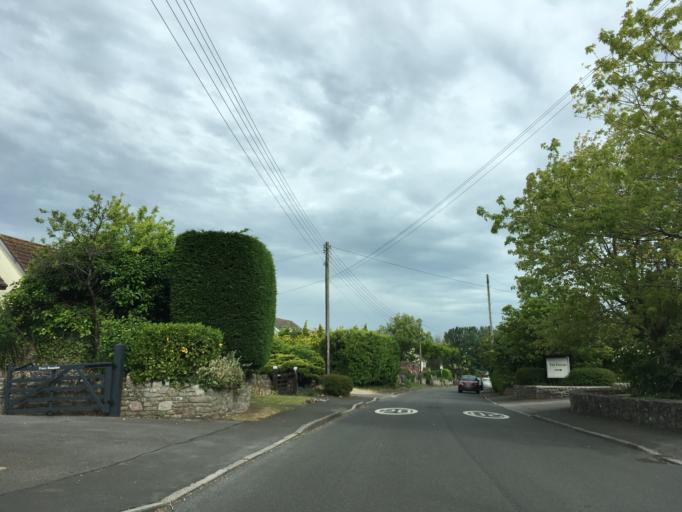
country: GB
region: England
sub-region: North Somerset
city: Easton-in-Gordano
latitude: 51.4747
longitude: -2.7239
